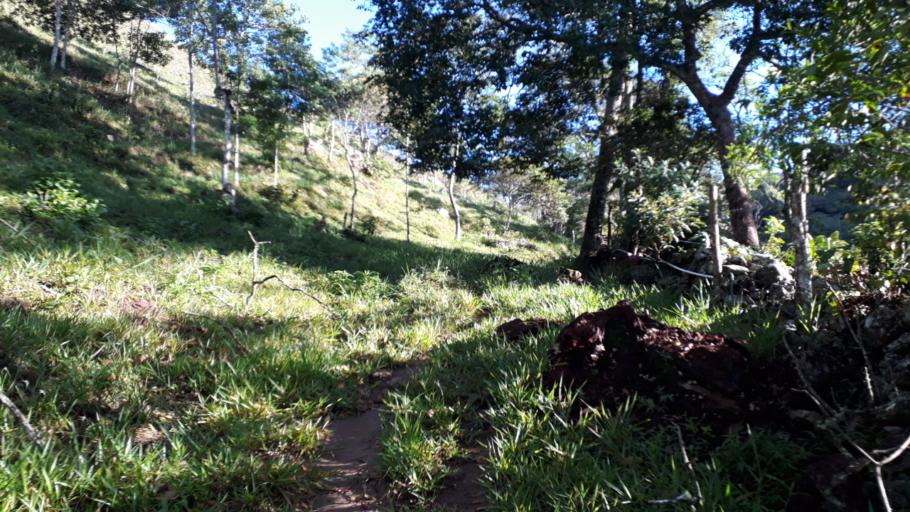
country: CO
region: Casanare
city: Nunchia
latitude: 5.6342
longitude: -72.4248
